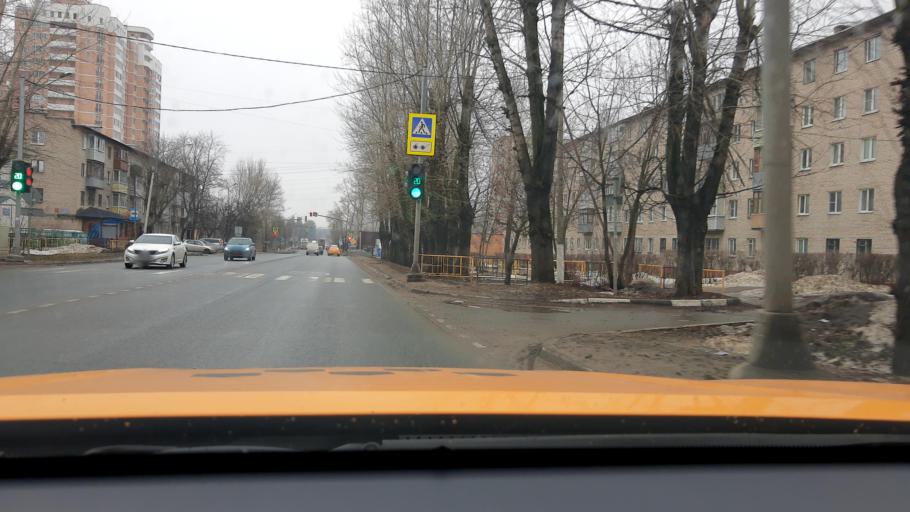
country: RU
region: Moskovskaya
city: Noginsk
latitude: 55.8778
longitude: 38.4305
